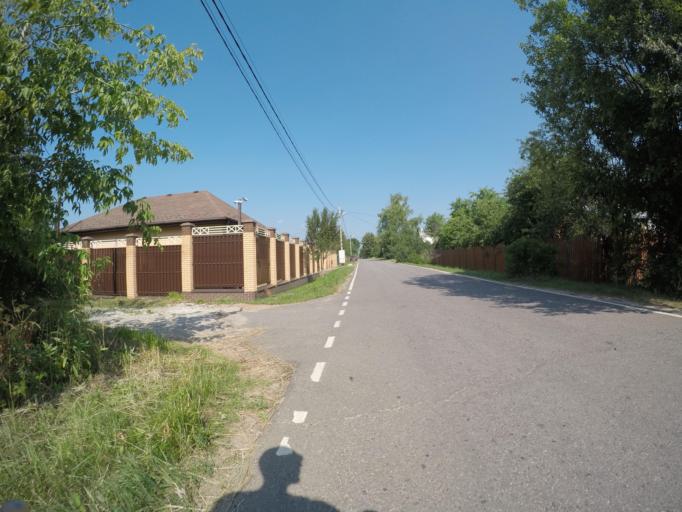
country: RU
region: Moskovskaya
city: Rechitsy
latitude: 55.6173
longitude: 38.5314
